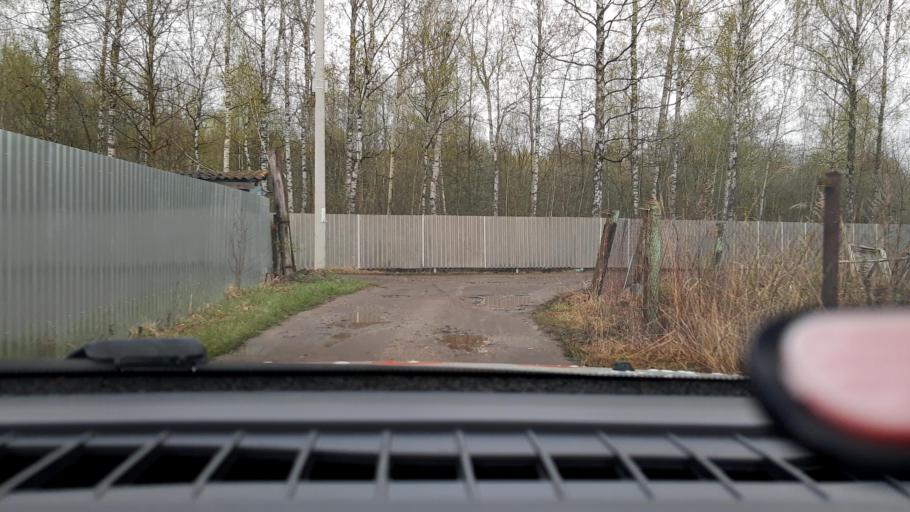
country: RU
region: Nizjnij Novgorod
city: Gorbatovka
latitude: 56.2992
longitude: 43.7693
